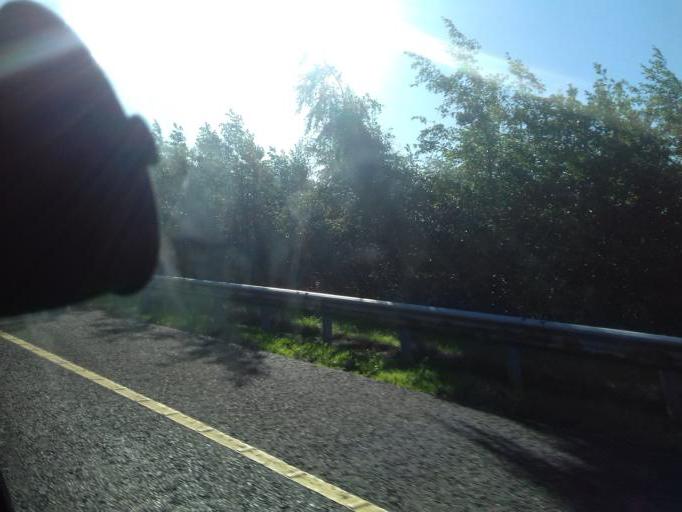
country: IE
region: Leinster
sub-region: An Iarmhi
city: Kilbeggan
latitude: 53.3601
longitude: -7.4298
